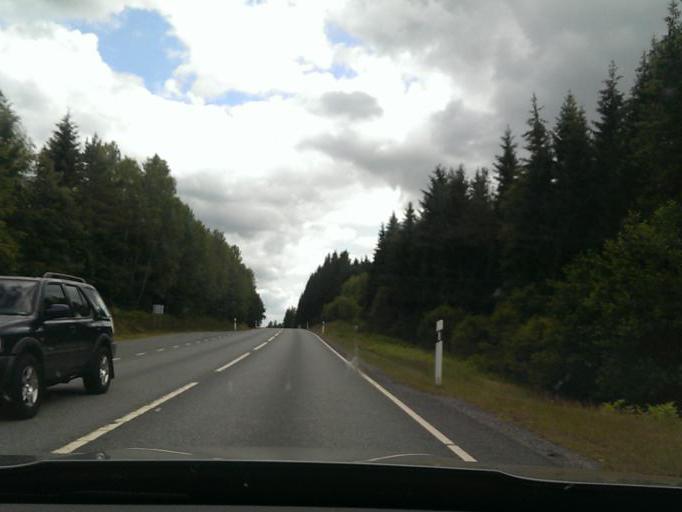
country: SE
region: Joenkoeping
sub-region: Varnamo Kommun
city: Varnamo
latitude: 57.2175
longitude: 14.0157
